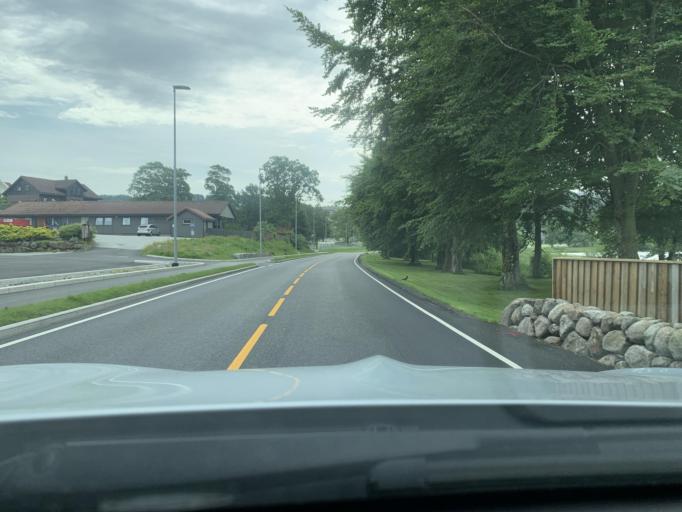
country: NO
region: Rogaland
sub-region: Sandnes
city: Sandnes
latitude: 58.7750
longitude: 5.7235
